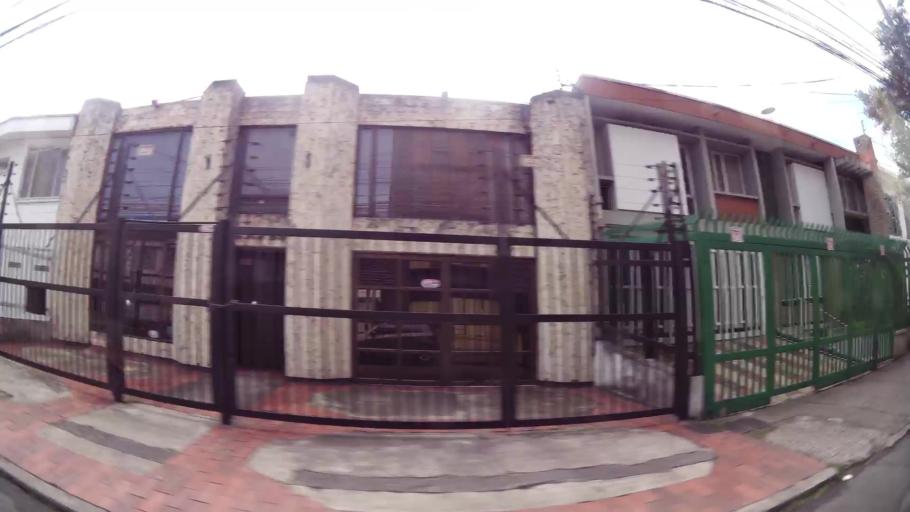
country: CO
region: Bogota D.C.
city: Barrio San Luis
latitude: 4.6813
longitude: -74.0591
